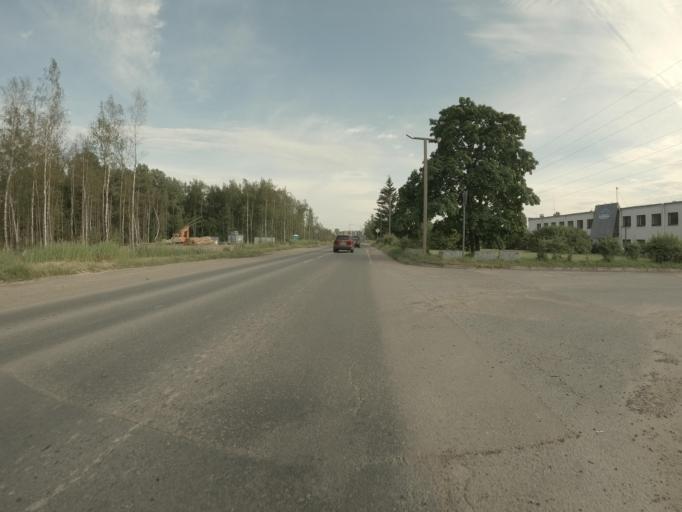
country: RU
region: St.-Petersburg
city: Krasnogvargeisky
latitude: 59.9307
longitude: 30.5203
